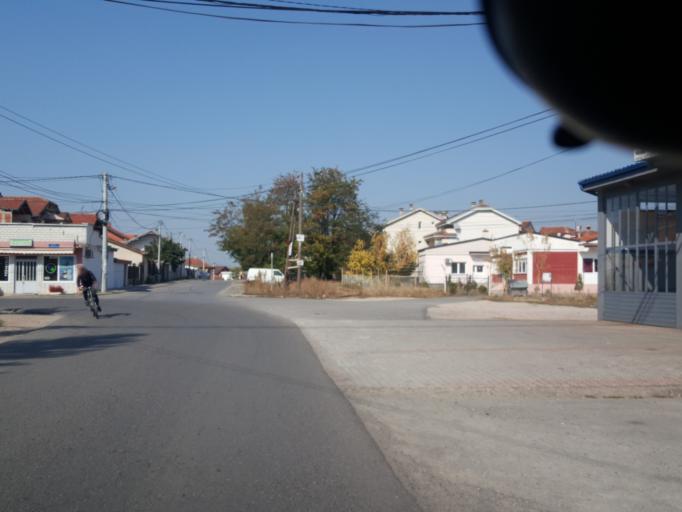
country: XK
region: Gjakova
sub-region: Komuna e Gjakoves
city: Gjakove
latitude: 42.3917
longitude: 20.4293
